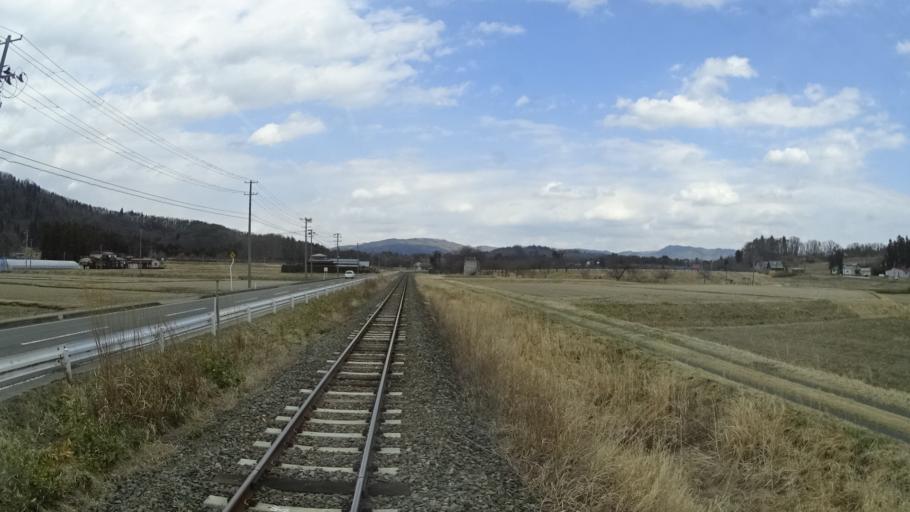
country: JP
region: Iwate
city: Hanamaki
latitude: 39.4083
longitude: 141.1862
